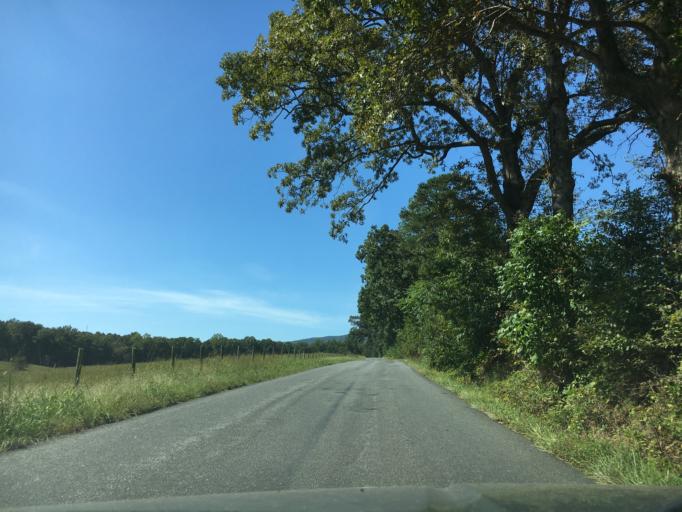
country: US
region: Virginia
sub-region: Albemarle County
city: Crozet
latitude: 38.0199
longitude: -78.7749
